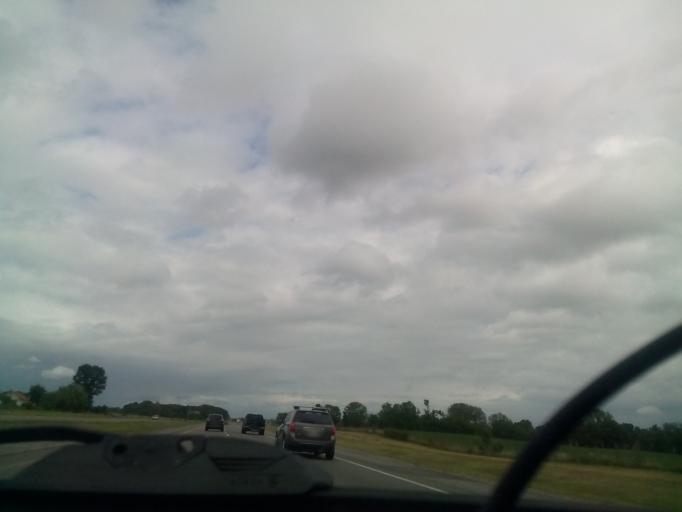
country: US
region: Ohio
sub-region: Williams County
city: Montpelier
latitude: 41.6276
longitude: -84.7216
